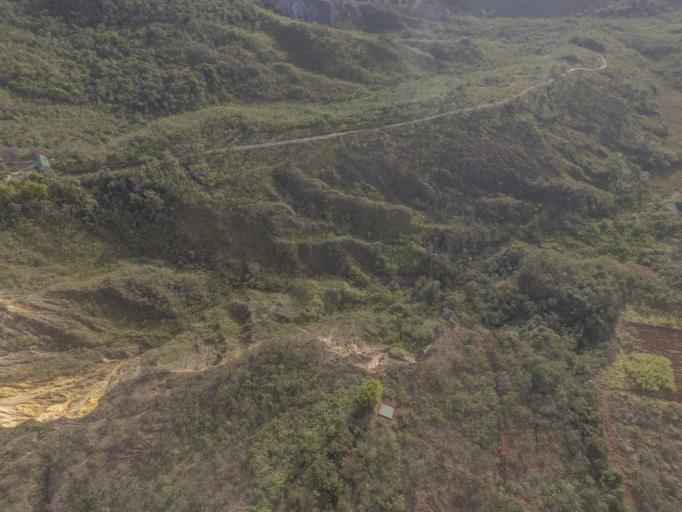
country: BR
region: Minas Gerais
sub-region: Tiradentes
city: Tiradentes
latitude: -21.0577
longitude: -44.1009
